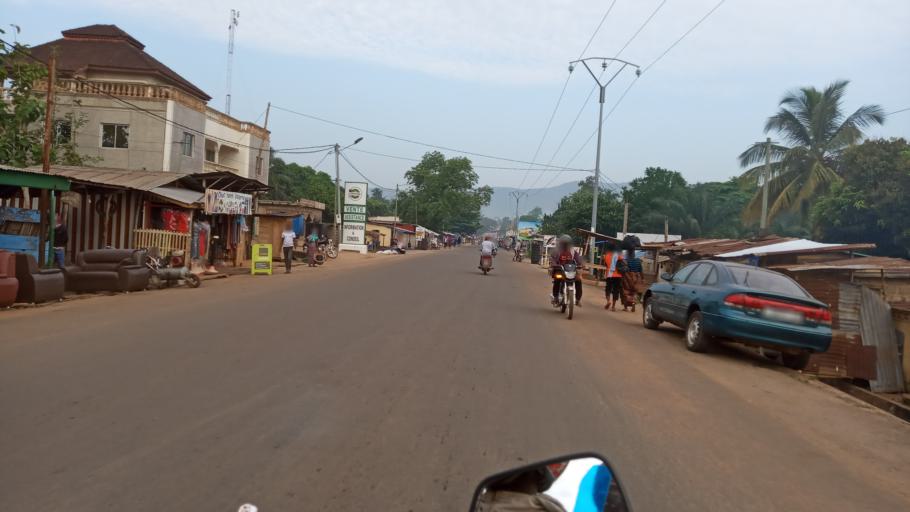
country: TG
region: Plateaux
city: Kpalime
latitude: 6.9001
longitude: 0.6350
